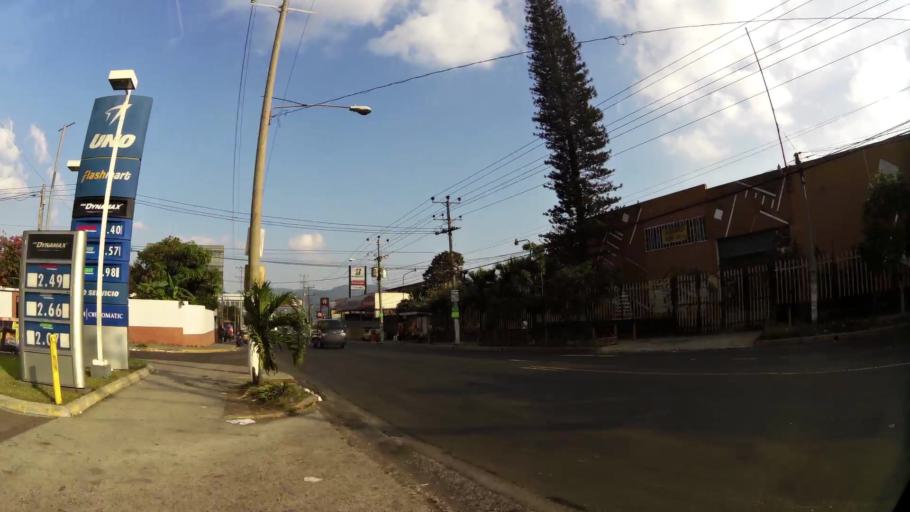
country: SV
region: San Salvador
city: San Salvador
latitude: 13.6932
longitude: -89.2204
